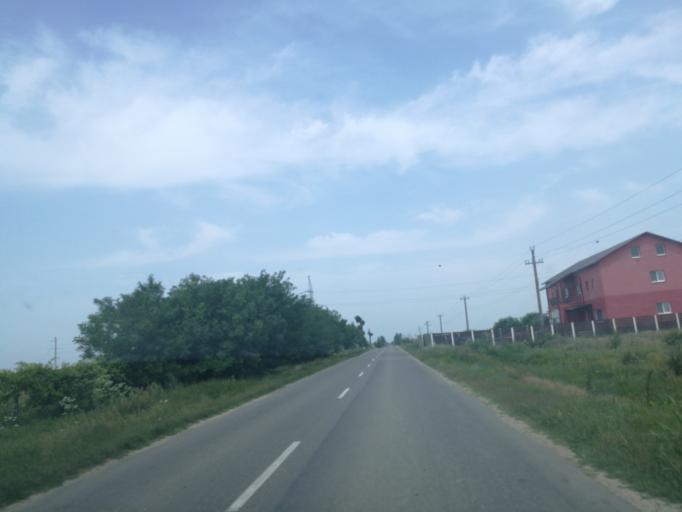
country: RO
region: Ilfov
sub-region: Comuna Vidra
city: Vidra
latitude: 44.2738
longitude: 26.1733
